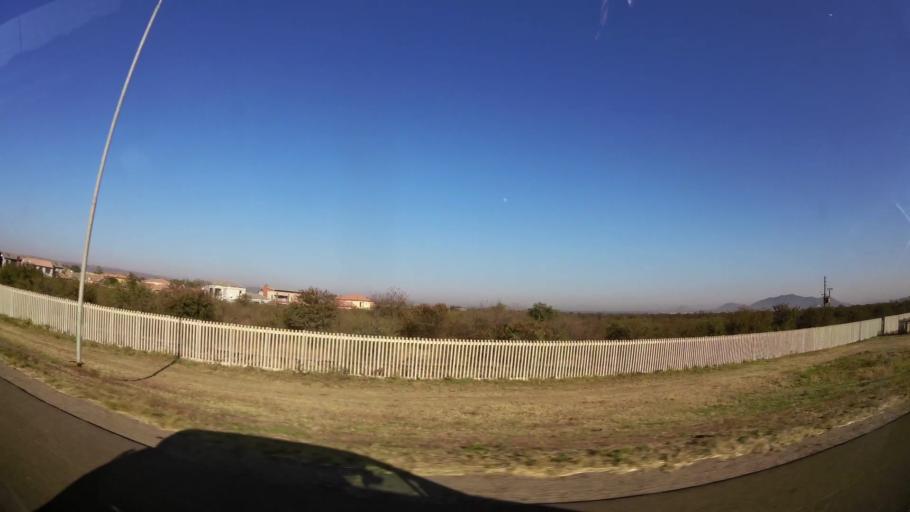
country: ZA
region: Gauteng
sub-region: City of Tshwane Metropolitan Municipality
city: Pretoria
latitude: -25.6491
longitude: 28.2738
